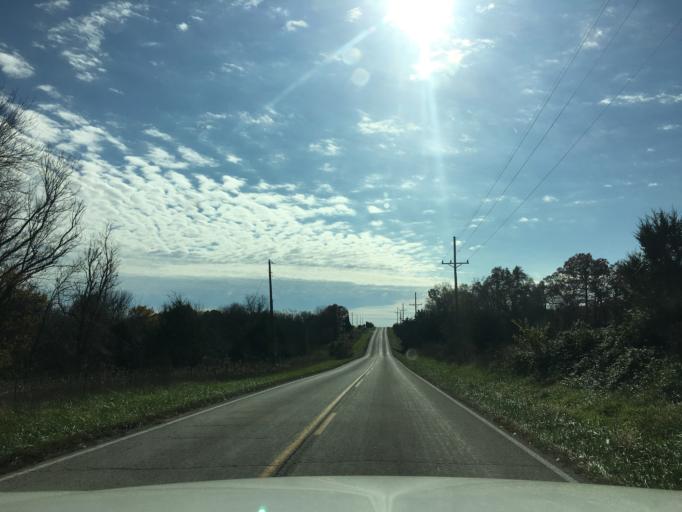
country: US
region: Missouri
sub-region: Osage County
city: Linn
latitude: 38.4054
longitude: -91.8179
